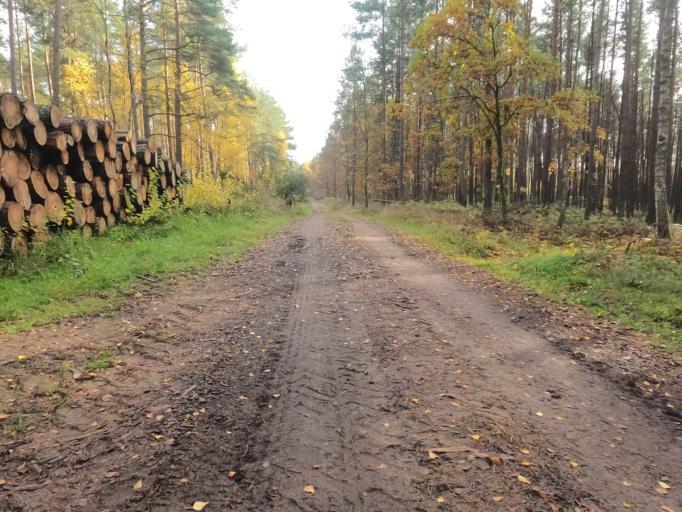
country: PL
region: West Pomeranian Voivodeship
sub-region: Powiat szczecinecki
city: Lubowo
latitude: 53.5550
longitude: 16.4215
